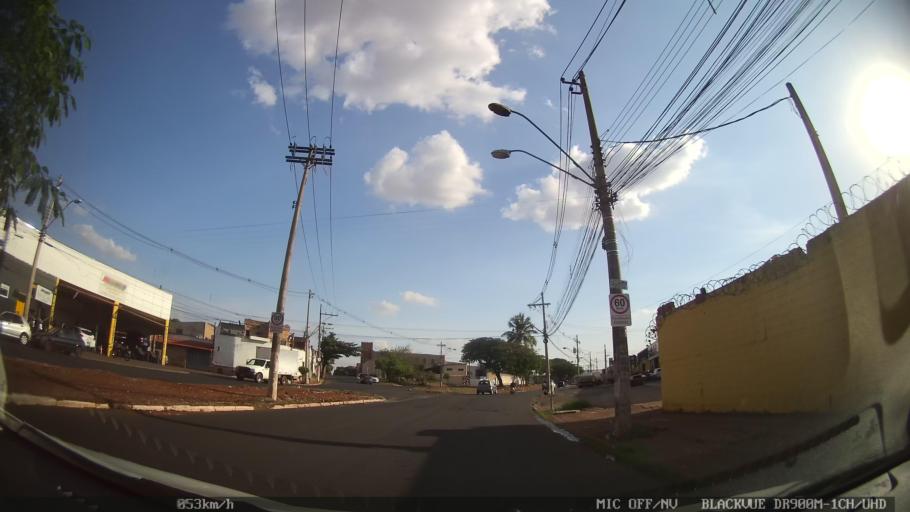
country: BR
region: Sao Paulo
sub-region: Ribeirao Preto
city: Ribeirao Preto
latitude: -21.1477
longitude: -47.8007
